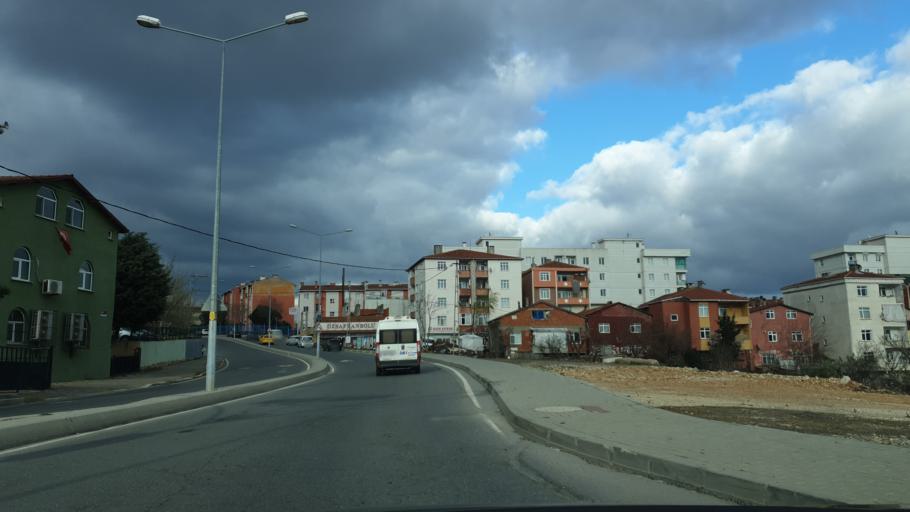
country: TR
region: Istanbul
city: Pendik
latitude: 40.9132
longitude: 29.2526
